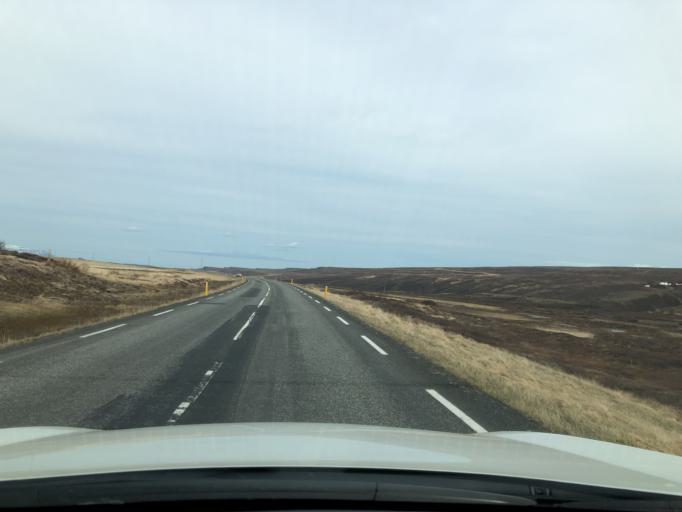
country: IS
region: East
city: Egilsstadir
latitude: 65.4127
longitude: -14.6265
